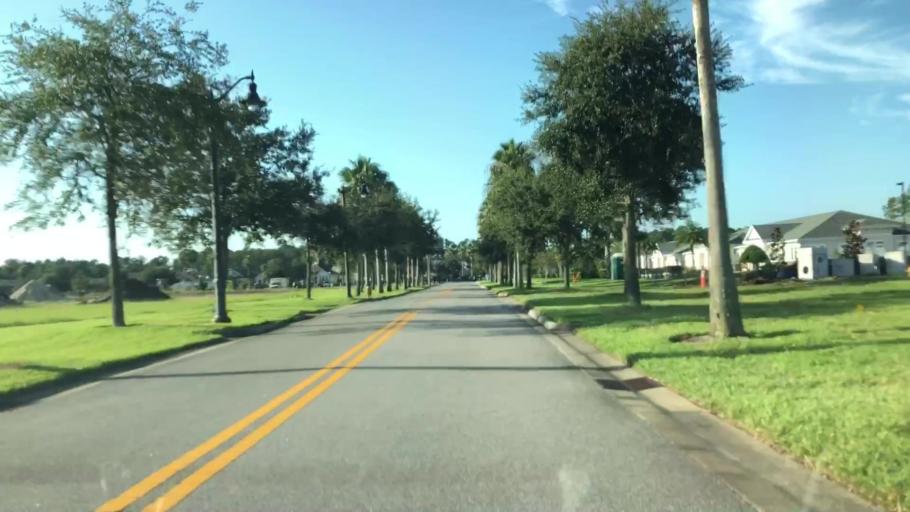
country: US
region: Florida
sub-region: Saint Johns County
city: Palm Valley
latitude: 30.1102
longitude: -81.4212
